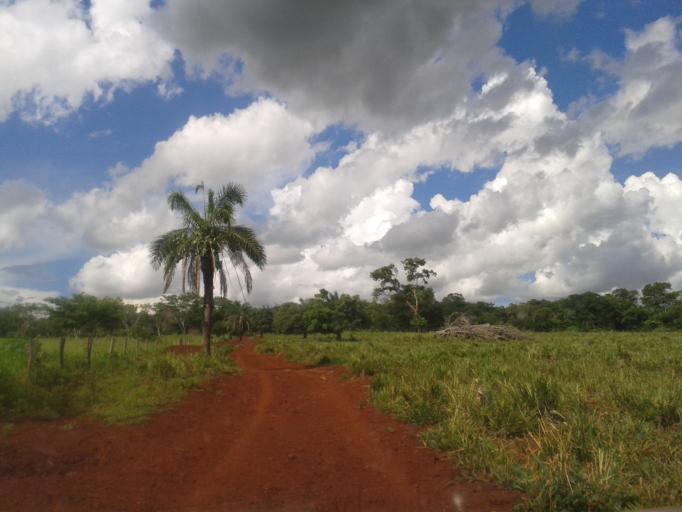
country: BR
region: Minas Gerais
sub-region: Capinopolis
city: Capinopolis
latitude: -18.7688
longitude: -49.8279
